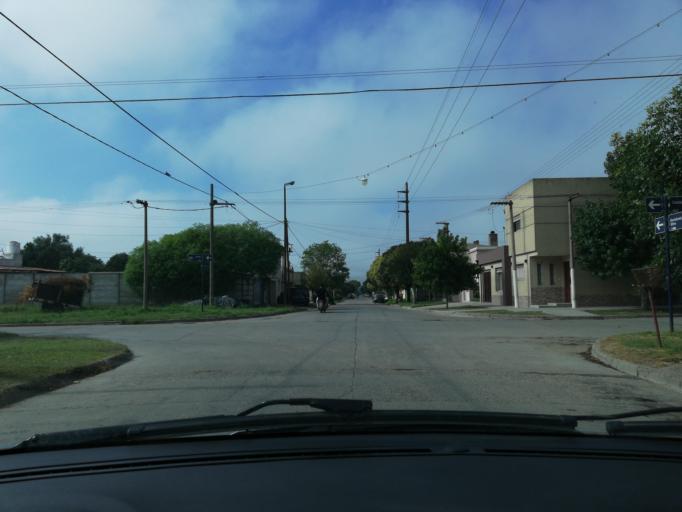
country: AR
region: Buenos Aires
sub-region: Partido de Balcarce
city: Balcarce
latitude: -37.8539
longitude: -58.2481
